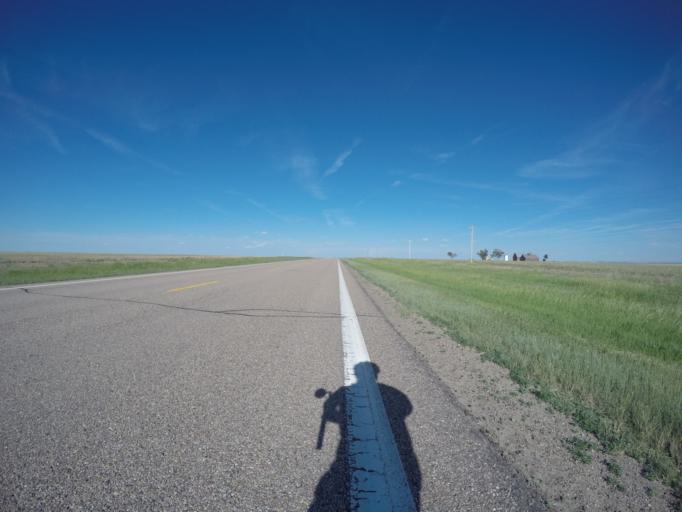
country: US
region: Kansas
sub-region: Cheyenne County
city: Saint Francis
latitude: 39.7565
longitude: -101.9890
